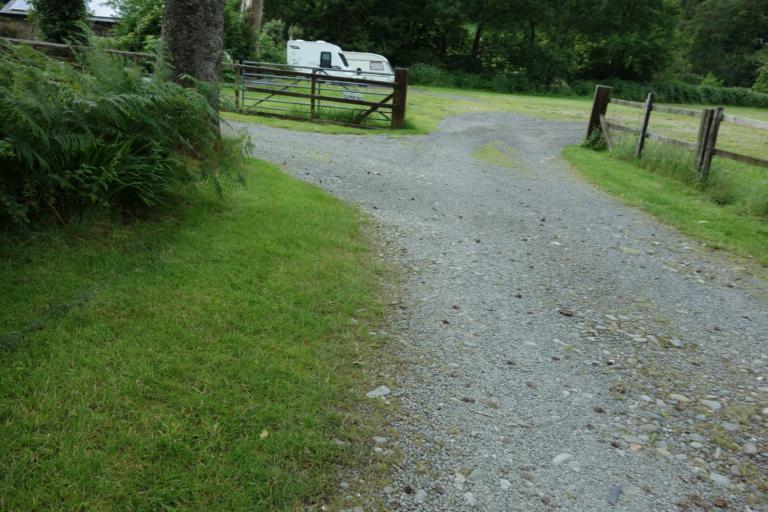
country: GB
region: Wales
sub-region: Gwynedd
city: Corris
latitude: 52.6844
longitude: -3.8812
